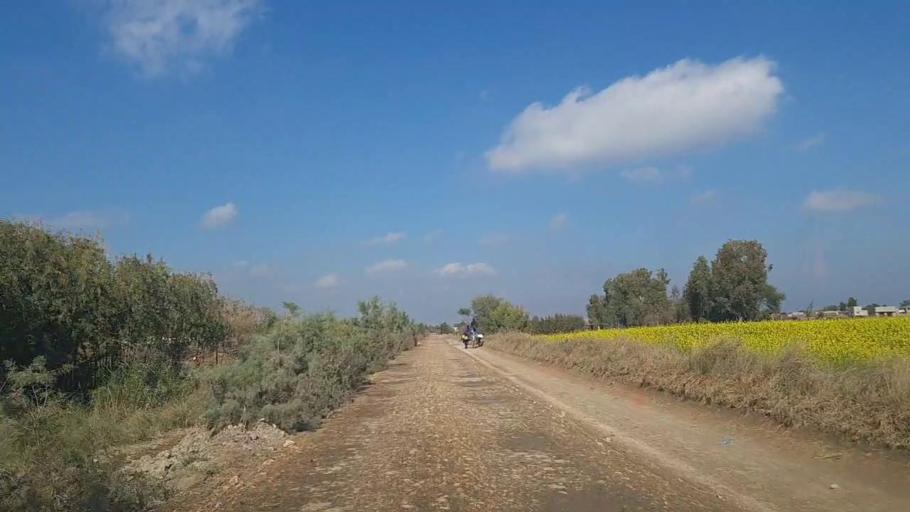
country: PK
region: Sindh
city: Sanghar
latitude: 26.0744
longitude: 68.9865
